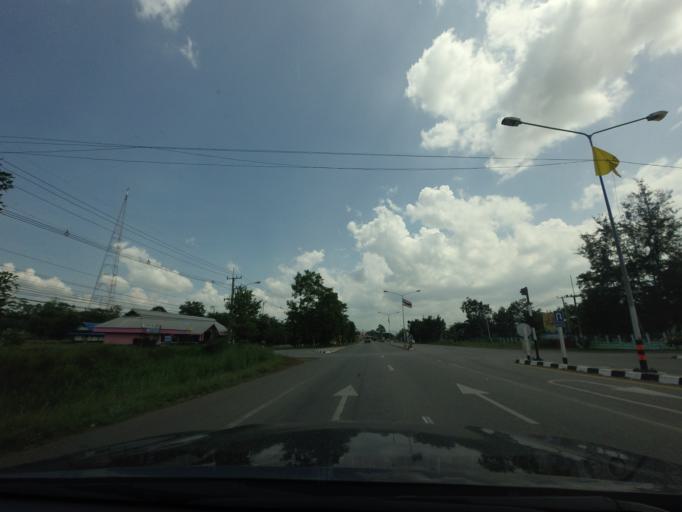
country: TH
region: Phetchabun
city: Phetchabun
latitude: 16.2504
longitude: 101.0681
